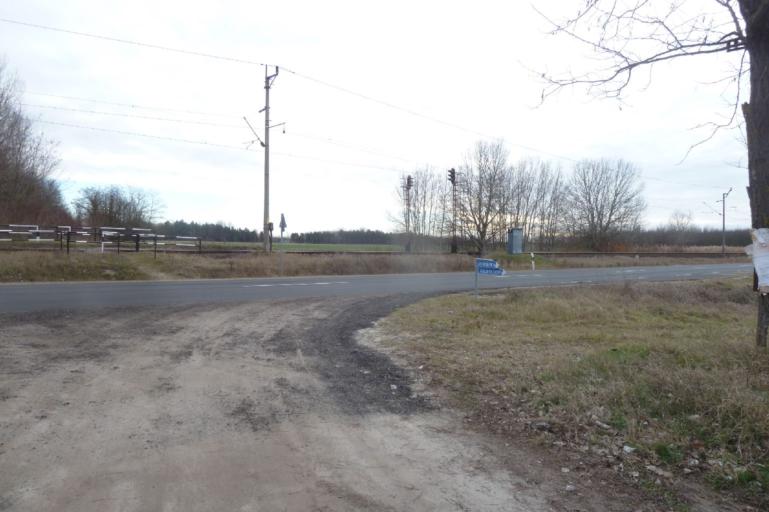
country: HU
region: Bacs-Kiskun
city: Jaszszentlaszlo
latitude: 46.5914
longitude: 19.7816
